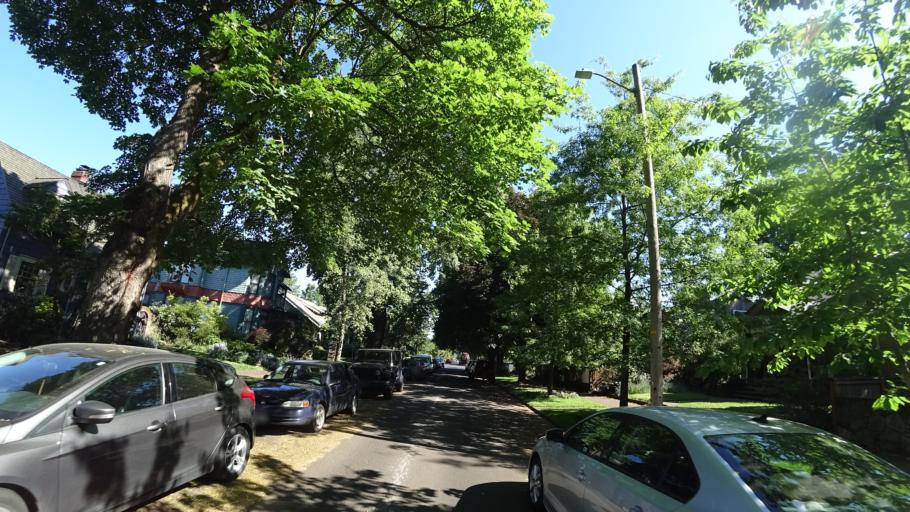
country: US
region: Oregon
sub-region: Multnomah County
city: Portland
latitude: 45.5657
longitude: -122.6648
